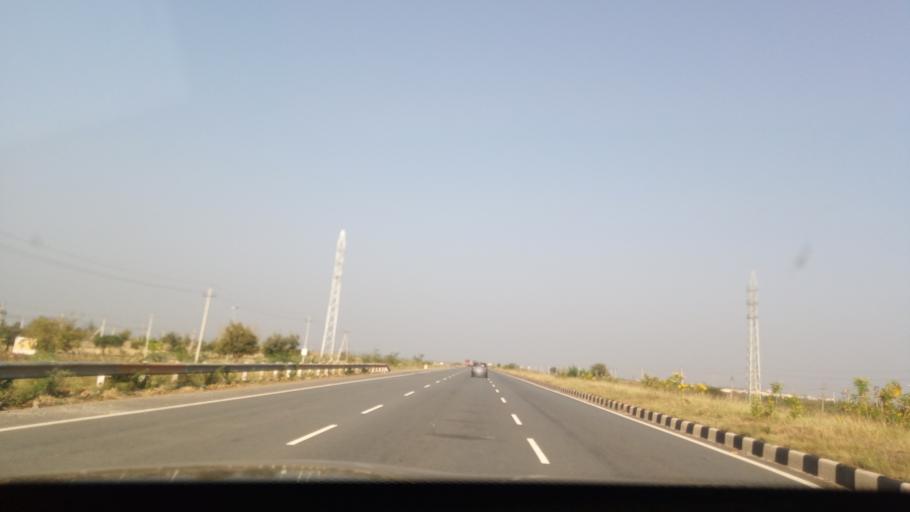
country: IN
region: Karnataka
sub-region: Haveri
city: Ranibennur
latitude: 14.5909
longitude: 75.6485
